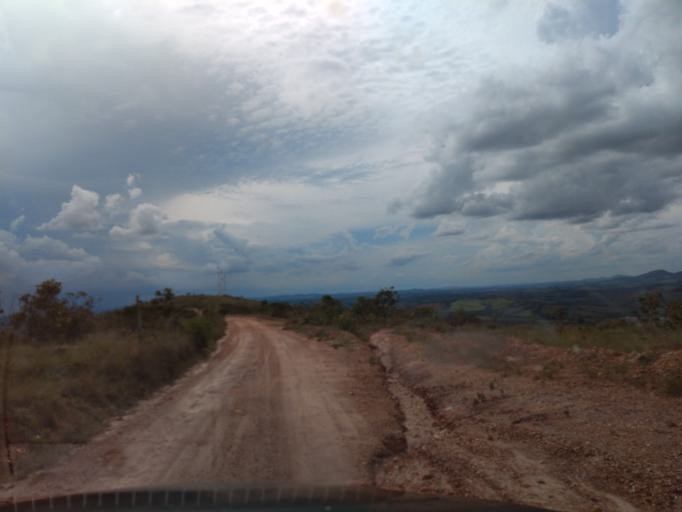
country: BR
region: Minas Gerais
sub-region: Lavras
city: Lavras
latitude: -21.5285
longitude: -44.8920
